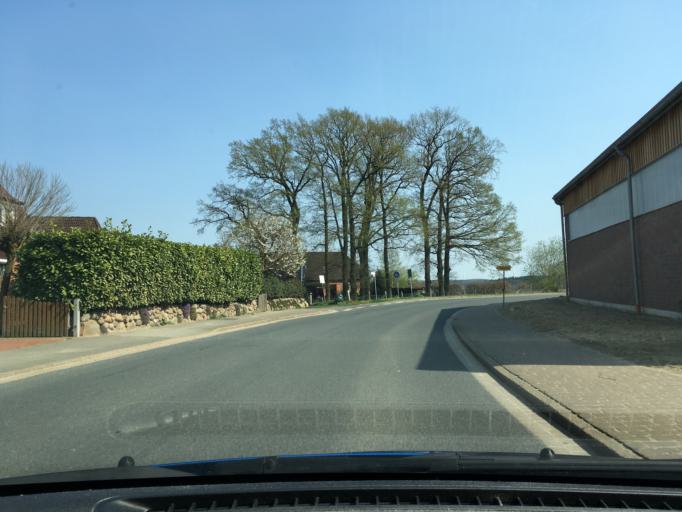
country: DE
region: Lower Saxony
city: Sudergellersen
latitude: 53.2079
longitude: 10.2990
